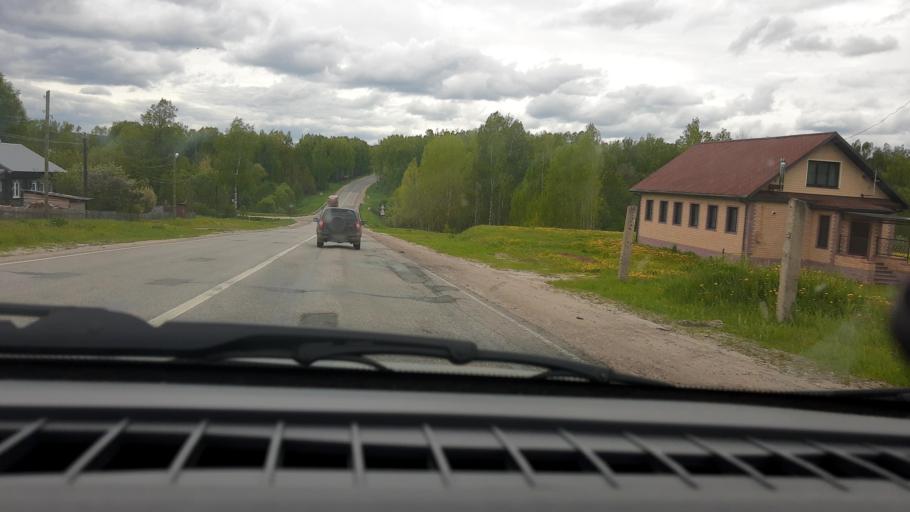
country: RU
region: Nizjnij Novgorod
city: Krasnyye Baki
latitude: 57.0652
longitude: 45.1375
